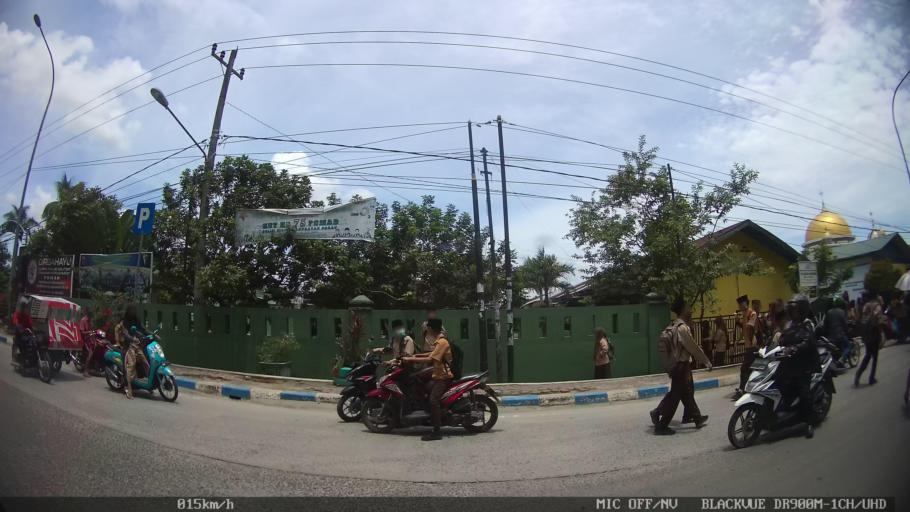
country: ID
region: North Sumatra
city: Percut
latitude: 3.5586
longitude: 98.8798
